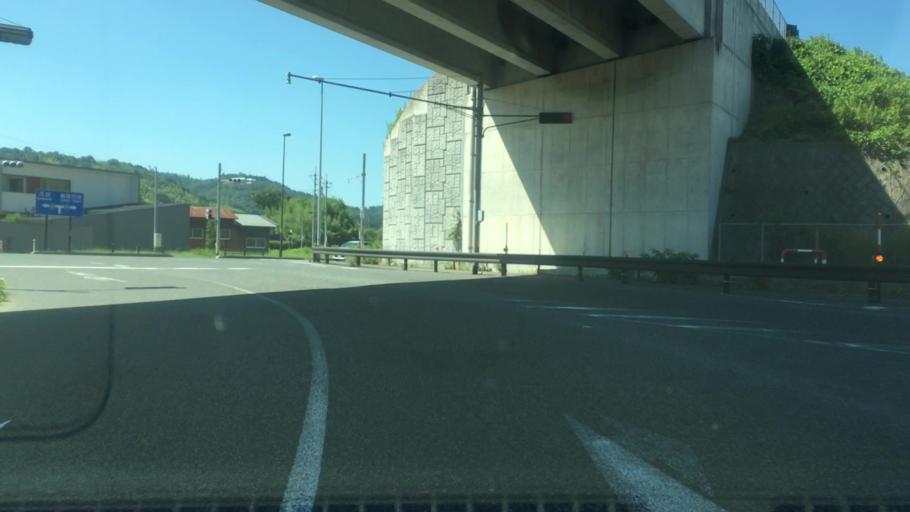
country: JP
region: Tottori
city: Tottori
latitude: 35.4244
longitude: 134.2075
